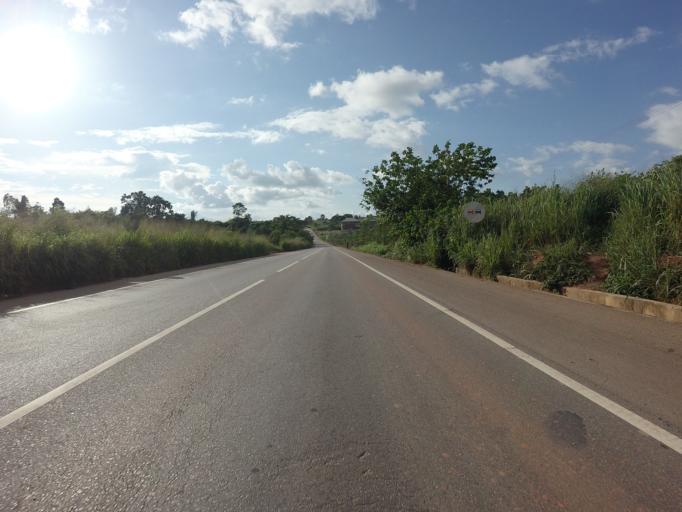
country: GH
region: Ashanti
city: Tafo
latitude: 6.8836
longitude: -1.6442
